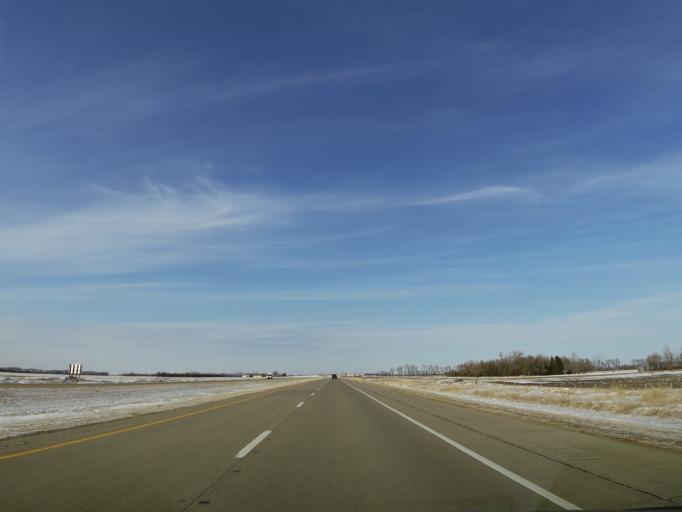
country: US
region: North Dakota
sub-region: Walsh County
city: Grafton
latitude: 48.4250
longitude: -97.1903
